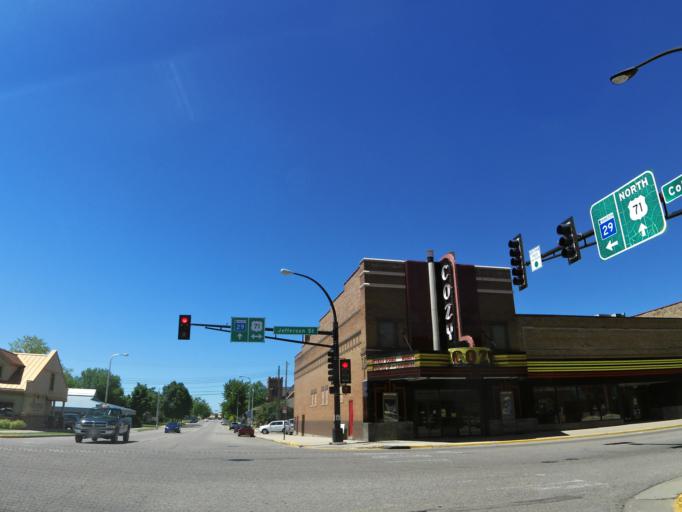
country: US
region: Minnesota
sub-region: Wadena County
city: Wadena
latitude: 46.4393
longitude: -95.1381
